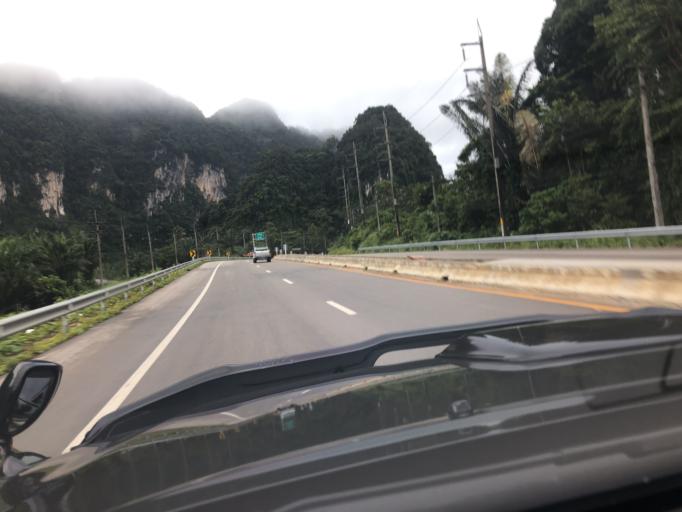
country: TH
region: Krabi
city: Ao Luek
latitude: 8.4111
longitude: 98.7379
